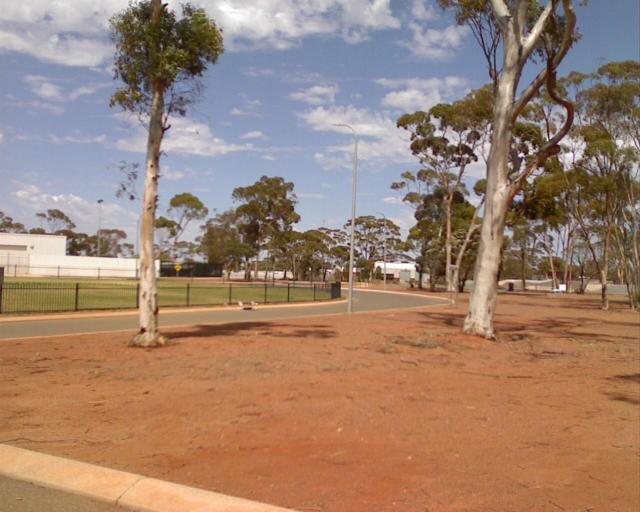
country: AU
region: Western Australia
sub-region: Kalgoorlie/Boulder
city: Stoneville
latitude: -31.2073
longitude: 121.6218
